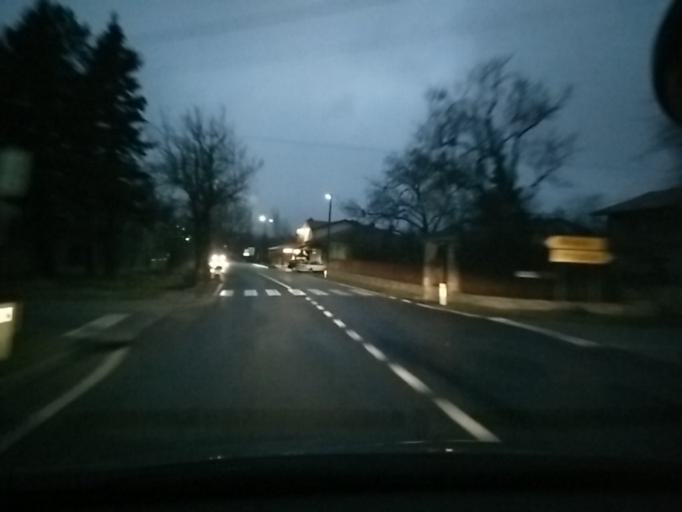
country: SI
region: Hrpelje-Kozina
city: Kozina
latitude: 45.6190
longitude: 13.9096
